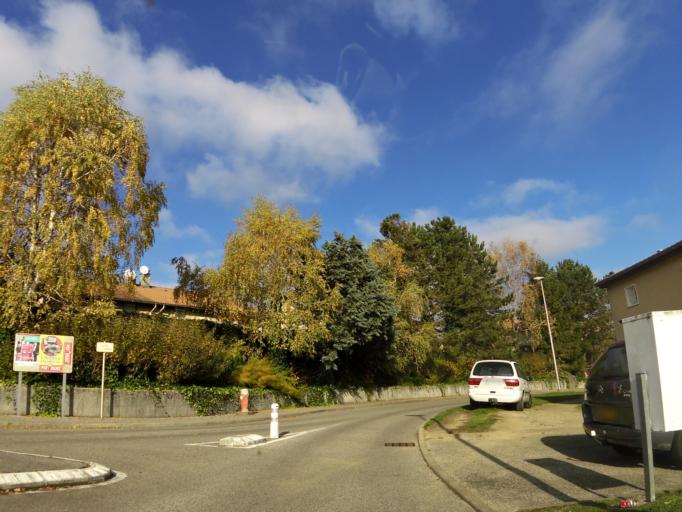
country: FR
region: Rhone-Alpes
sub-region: Departement de l'Ain
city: Meximieux
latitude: 45.9151
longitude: 5.1955
